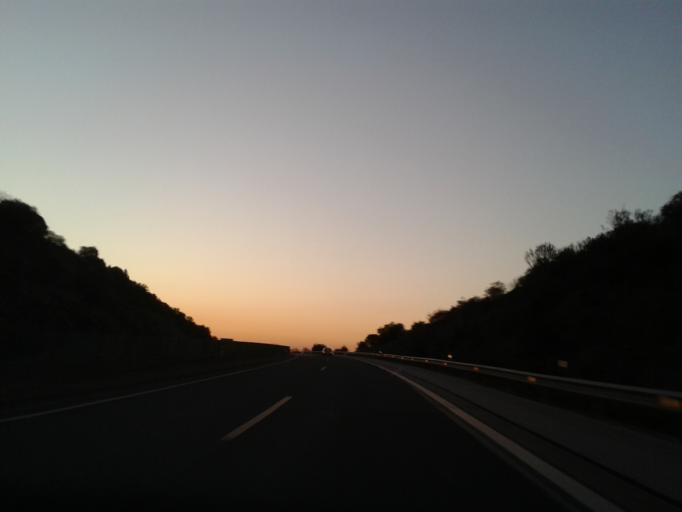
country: PT
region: Faro
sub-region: Loule
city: Boliqueime
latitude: 37.1553
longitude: -8.1780
